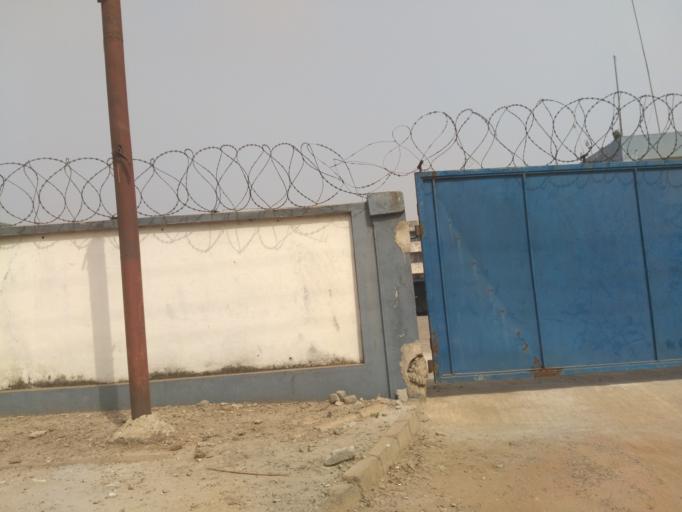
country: GH
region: Ashanti
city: Kumasi
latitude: 6.6913
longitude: -1.6063
